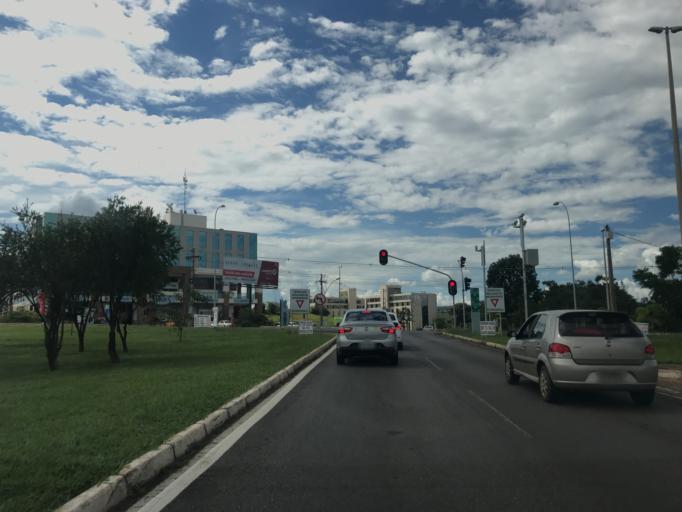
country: BR
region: Federal District
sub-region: Brasilia
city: Brasilia
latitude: -15.7229
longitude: -47.8815
